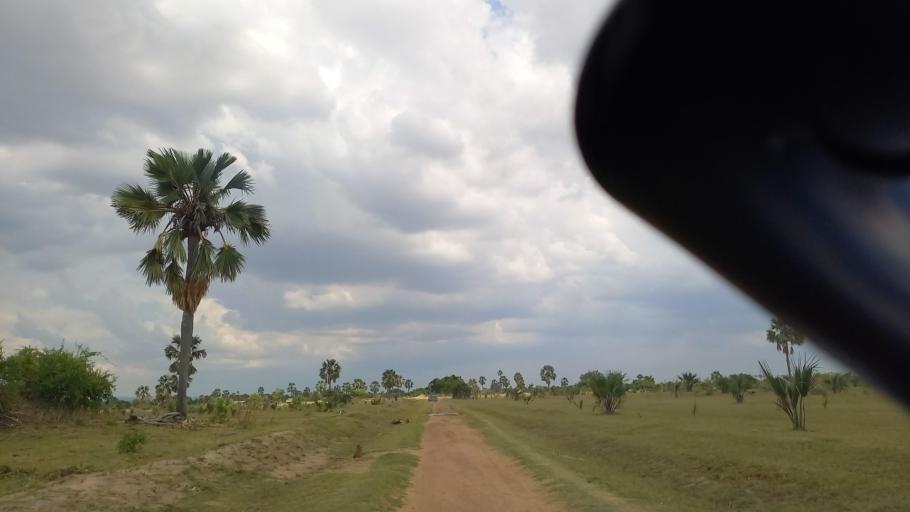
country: ZM
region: Lusaka
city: Kafue
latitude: -15.8270
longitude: 28.0515
